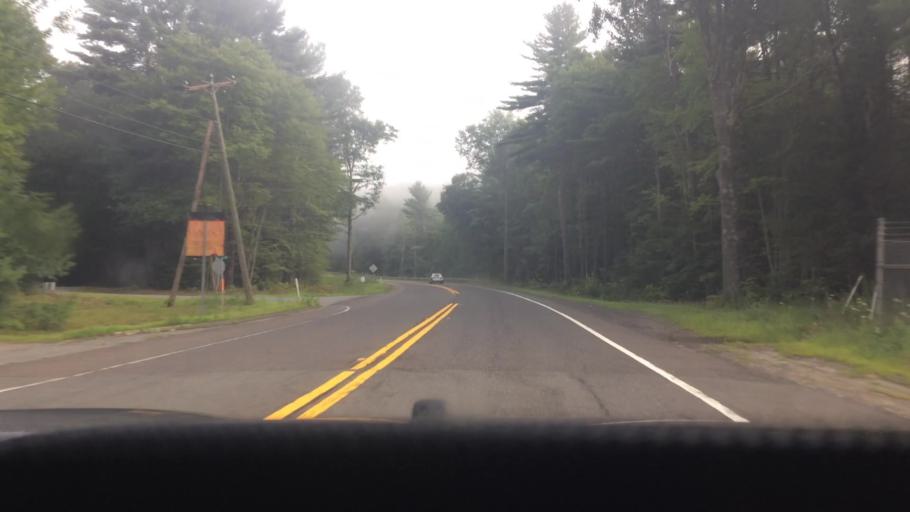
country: US
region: Massachusetts
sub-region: Franklin County
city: Millers Falls
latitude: 42.5924
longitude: -72.4906
